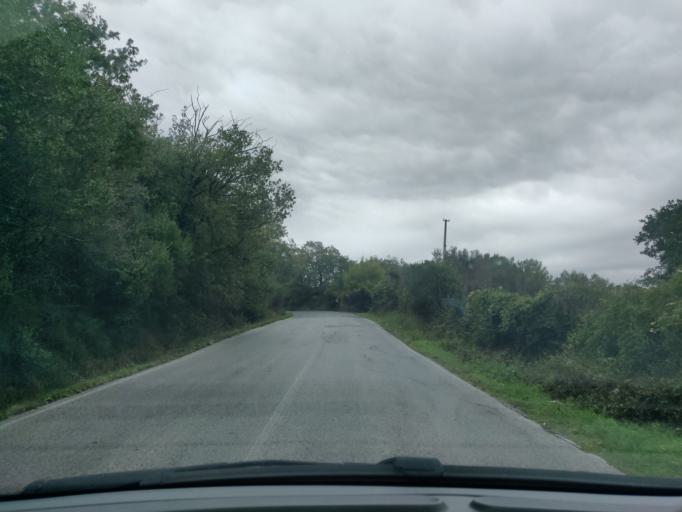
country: IT
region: Latium
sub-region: Citta metropolitana di Roma Capitale
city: Allumiere
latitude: 42.1318
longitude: 11.8687
